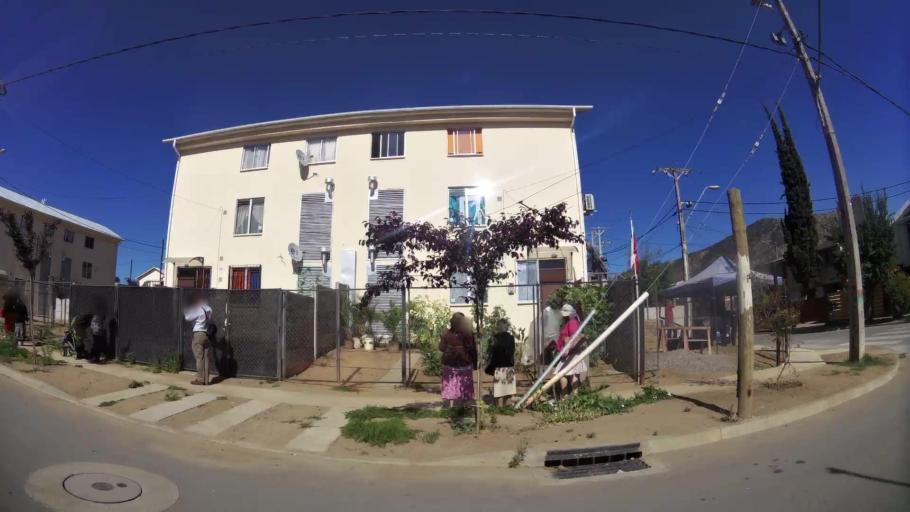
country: CL
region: Santiago Metropolitan
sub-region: Provincia de Chacabuco
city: Lampa
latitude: -33.4076
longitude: -71.1266
